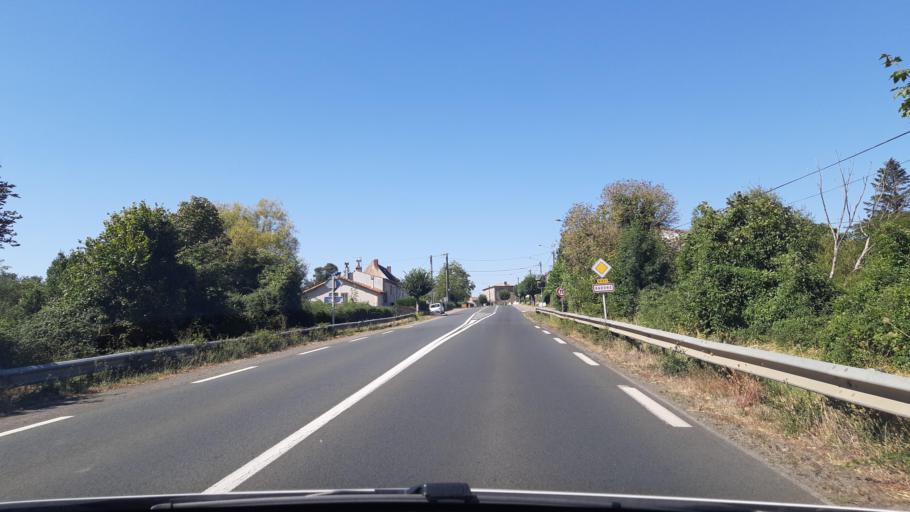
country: FR
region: Poitou-Charentes
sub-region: Departement des Deux-Sevres
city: Azay-le-Brule
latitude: 46.3925
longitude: -0.2562
